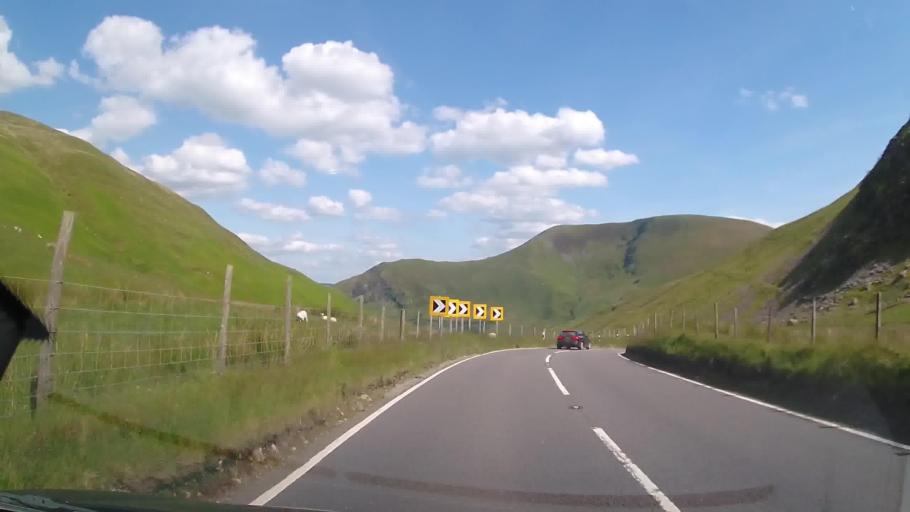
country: GB
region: Wales
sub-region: Gwynedd
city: Corris
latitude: 52.7377
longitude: -3.7744
